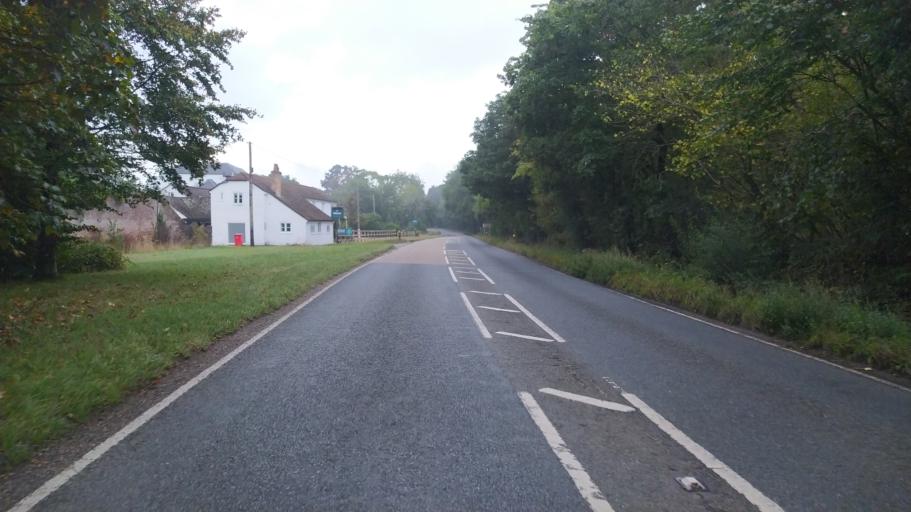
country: GB
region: England
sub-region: Hampshire
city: New Milton
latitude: 50.7723
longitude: -1.6965
